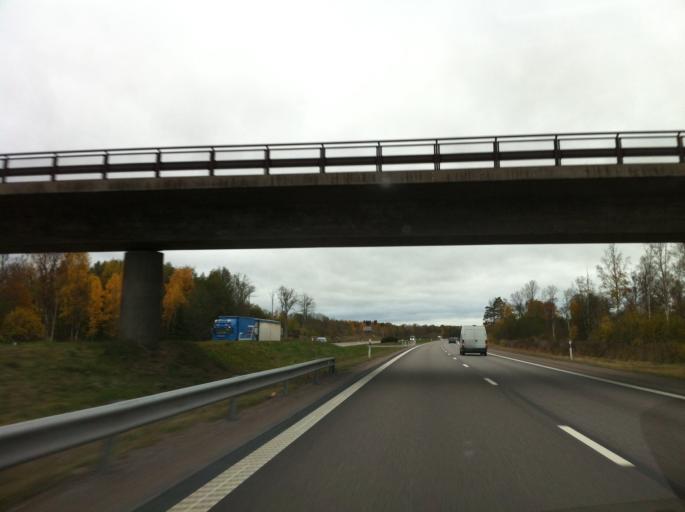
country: SE
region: OEstergoetland
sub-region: Mjolby Kommun
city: Mjolby
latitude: 58.3153
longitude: 15.0427
